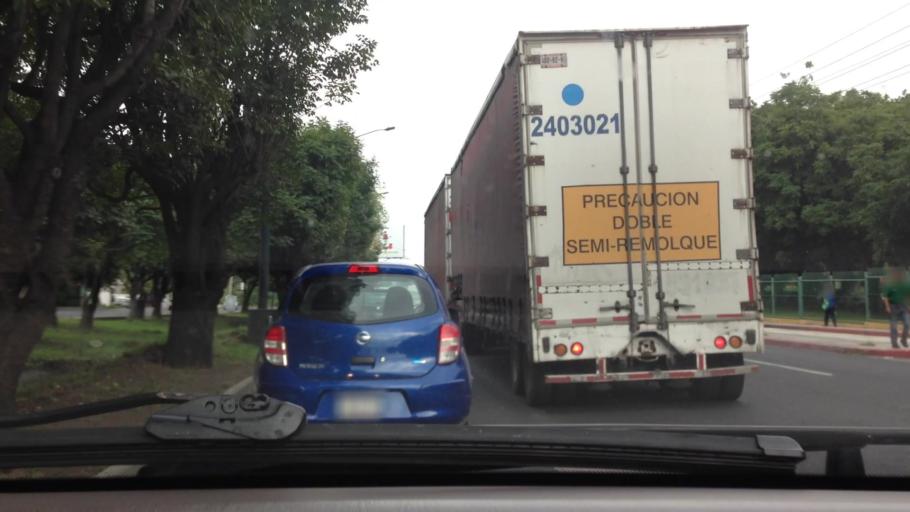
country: MX
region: Morelos
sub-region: Tepoztlan
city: Loma Bonita
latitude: 18.9189
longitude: -99.1904
